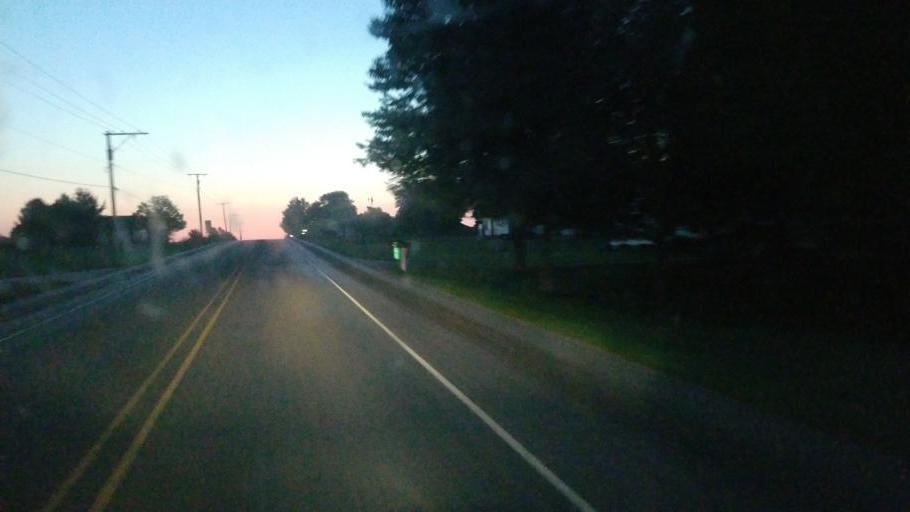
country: US
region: Indiana
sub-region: Elkhart County
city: Middlebury
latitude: 41.6757
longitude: -85.6603
